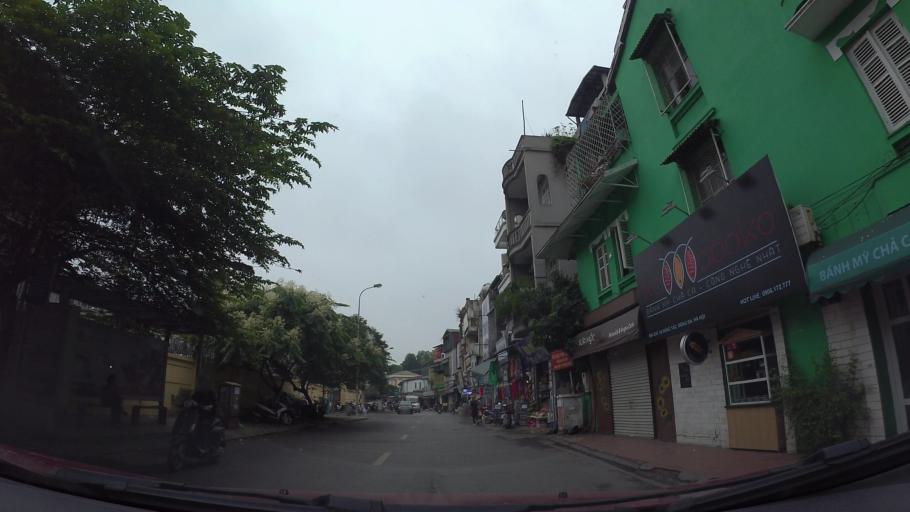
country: VN
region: Ha Noi
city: Dong Da
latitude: 21.0059
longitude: 105.8331
